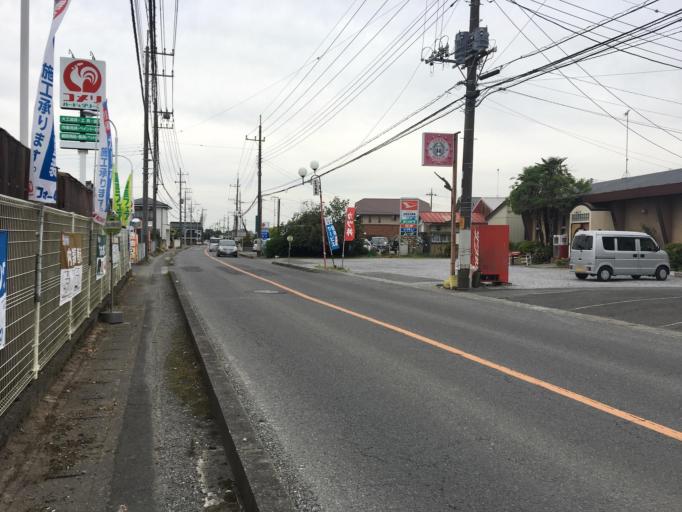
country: JP
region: Tochigi
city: Tochigi
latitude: 36.4213
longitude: 139.7497
